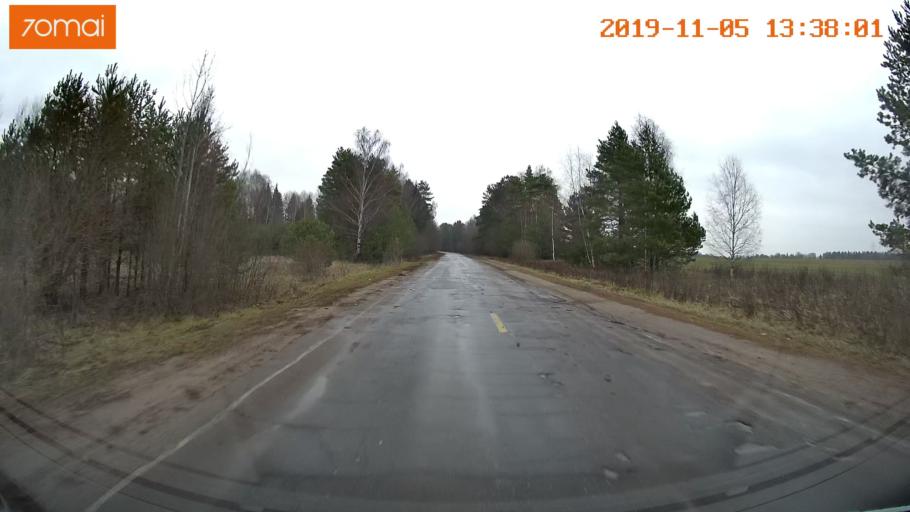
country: RU
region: Ivanovo
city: Shuya
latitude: 56.9281
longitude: 41.3833
